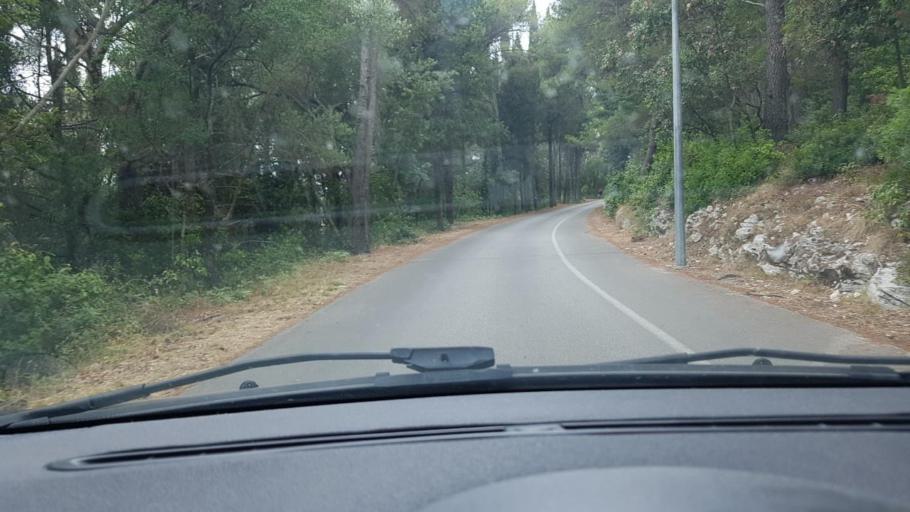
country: HR
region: Dubrovacko-Neretvanska
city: Korcula
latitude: 42.9569
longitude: 17.1312
